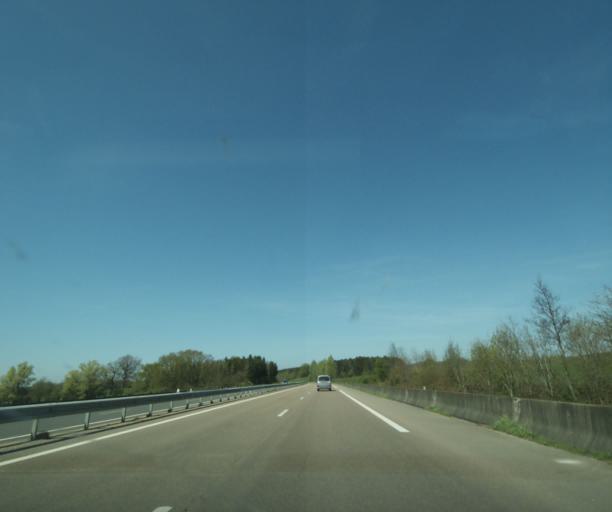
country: FR
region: Bourgogne
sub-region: Departement de la Nievre
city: Pougues-les-Eaux
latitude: 47.0893
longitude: 3.1020
